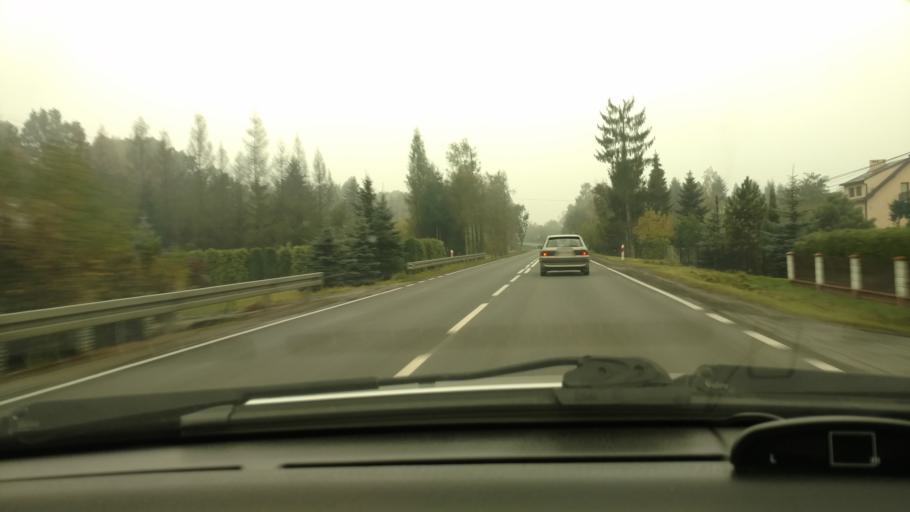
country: PL
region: Lesser Poland Voivodeship
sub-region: Powiat gorlicki
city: Kobylanka
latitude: 49.7029
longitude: 21.2217
